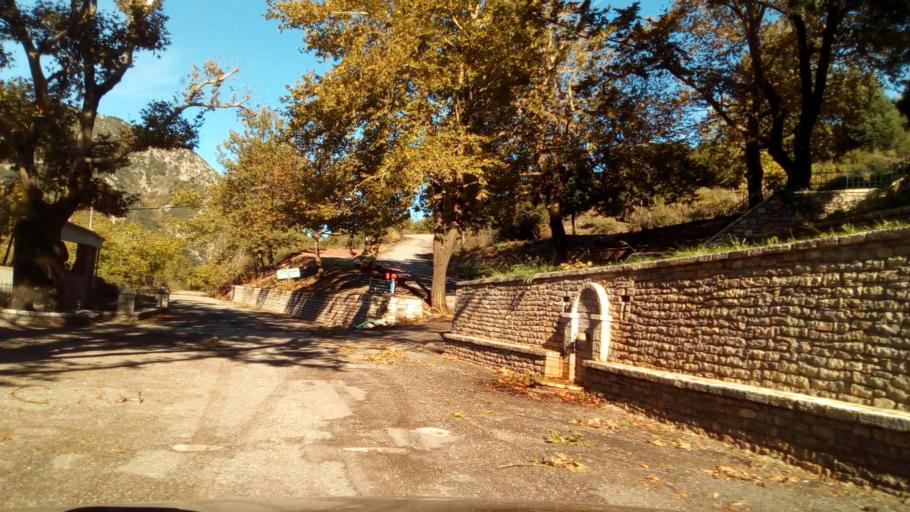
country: GR
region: West Greece
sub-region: Nomos Aitolias kai Akarnanias
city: Nafpaktos
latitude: 38.5582
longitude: 21.8556
